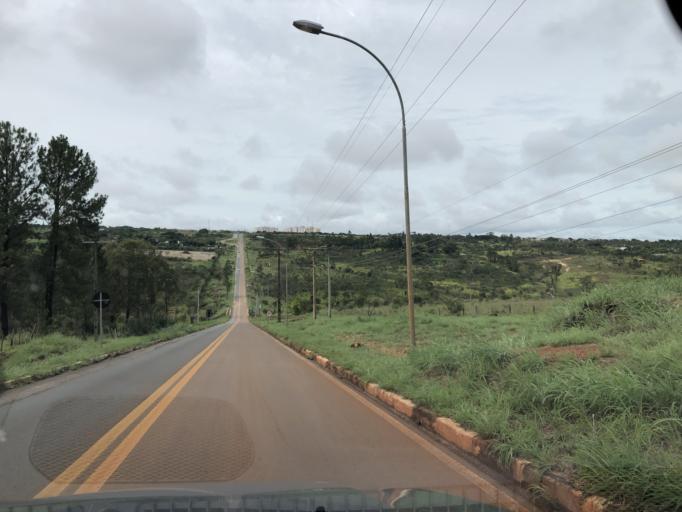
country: BR
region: Federal District
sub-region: Brasilia
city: Brasilia
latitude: -15.7669
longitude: -48.1283
